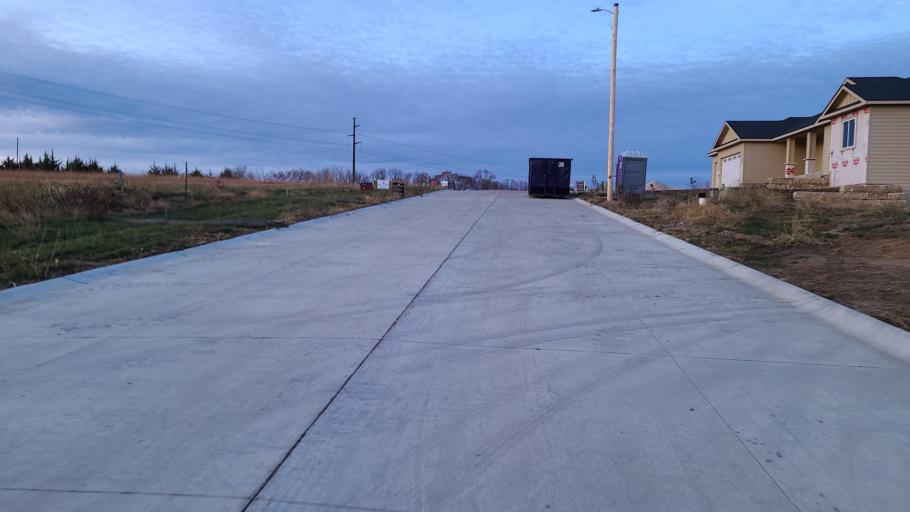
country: US
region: Kansas
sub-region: Riley County
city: Manhattan
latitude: 39.2215
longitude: -96.5094
